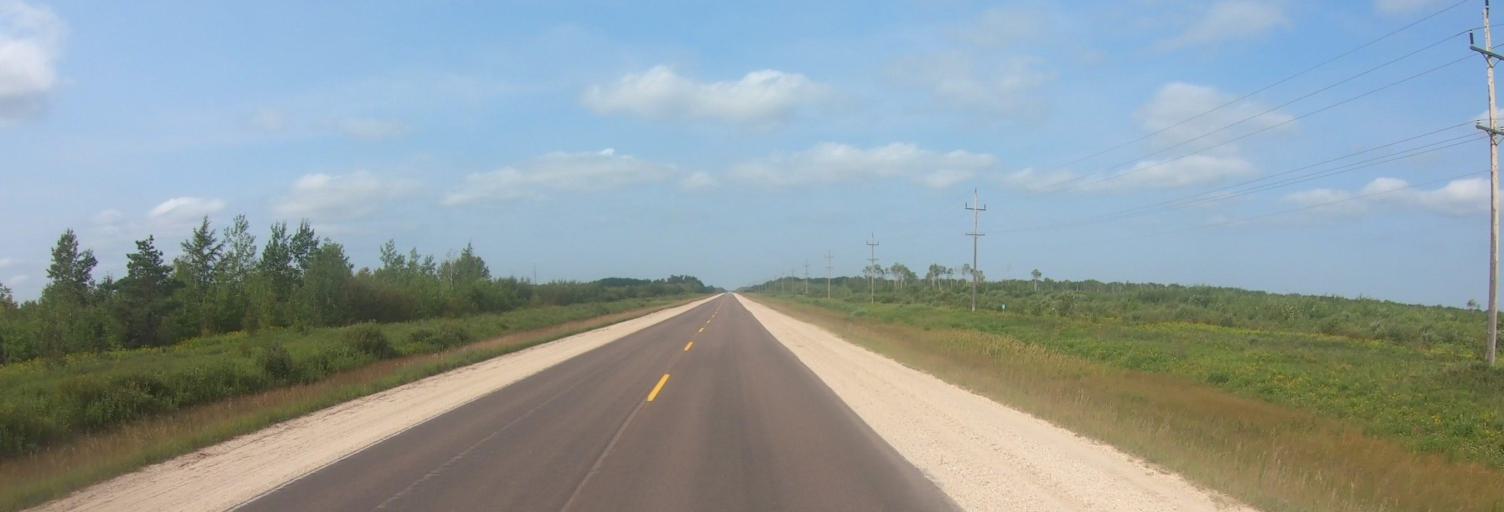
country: CA
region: Manitoba
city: La Broquerie
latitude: 49.2671
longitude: -96.3825
